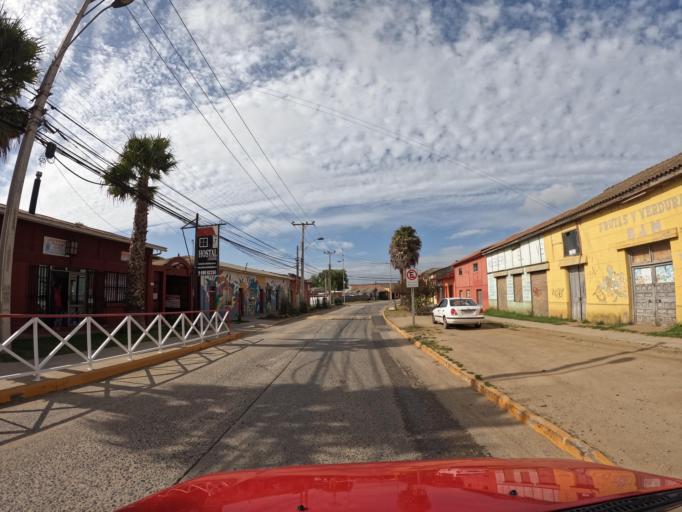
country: CL
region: O'Higgins
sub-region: Provincia de Colchagua
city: Santa Cruz
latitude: -34.3882
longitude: -72.0004
